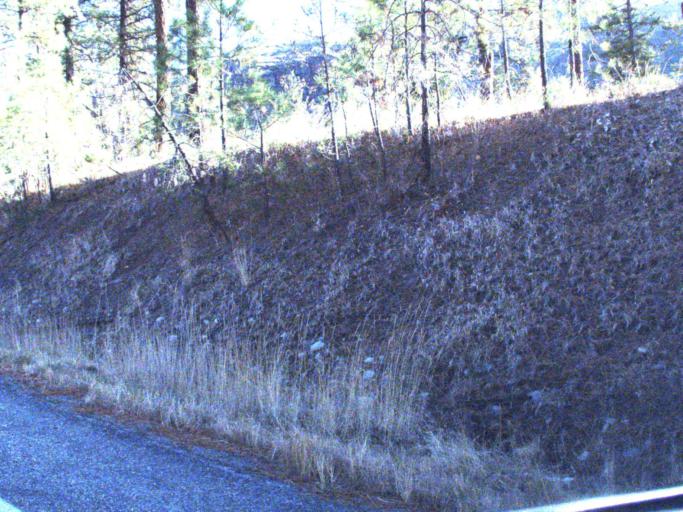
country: US
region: Washington
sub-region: Okanogan County
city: Coulee Dam
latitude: 48.0891
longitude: -118.6924
